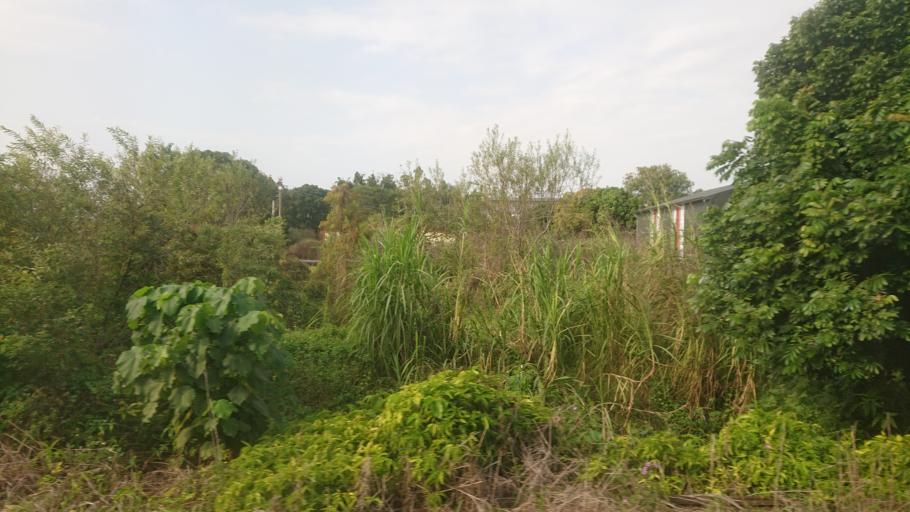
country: TW
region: Taiwan
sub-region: Nantou
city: Nantou
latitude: 23.8954
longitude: 120.5804
